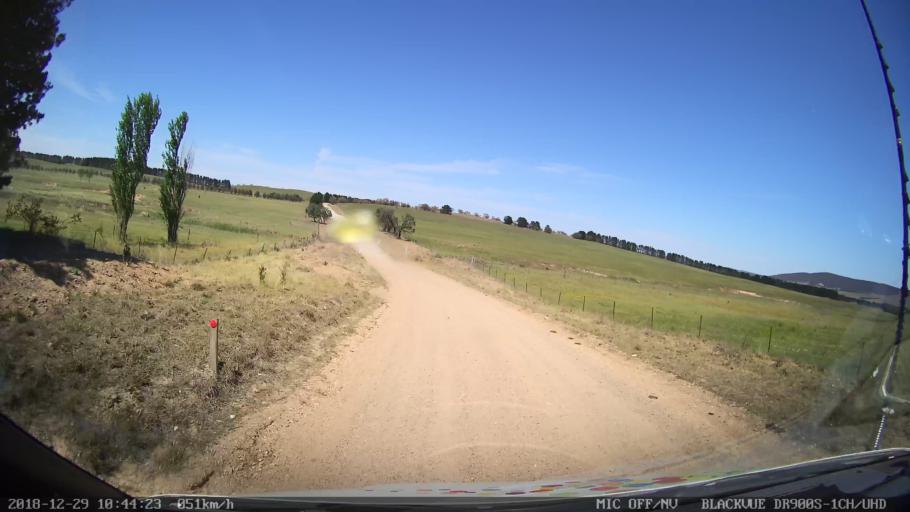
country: AU
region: New South Wales
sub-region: Palerang
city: Bungendore
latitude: -35.0416
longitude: 149.5289
